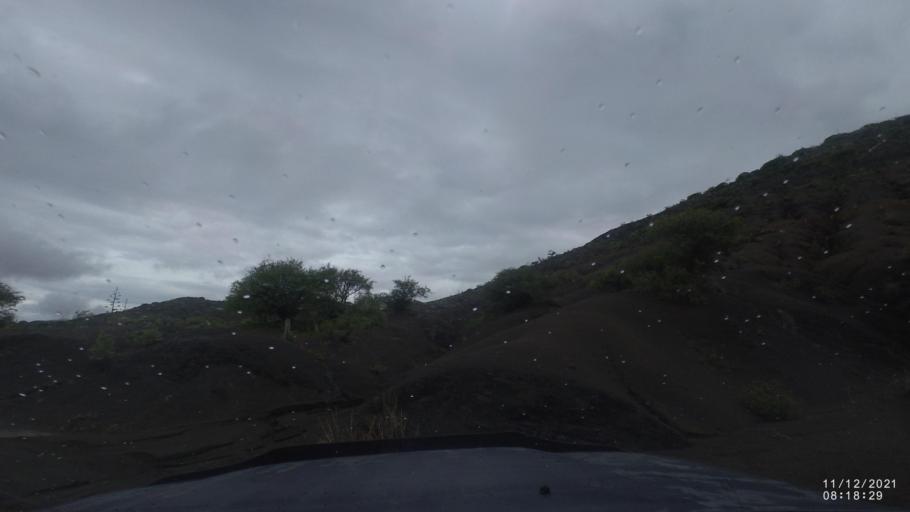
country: BO
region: Cochabamba
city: Tarata
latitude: -17.9413
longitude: -65.9295
